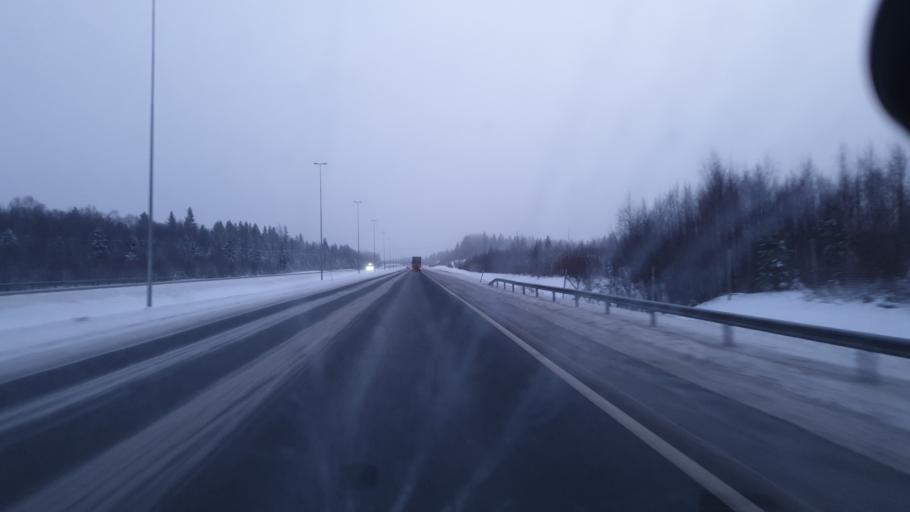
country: FI
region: Lapland
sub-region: Kemi-Tornio
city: Keminmaa
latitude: 65.8323
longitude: 24.3582
